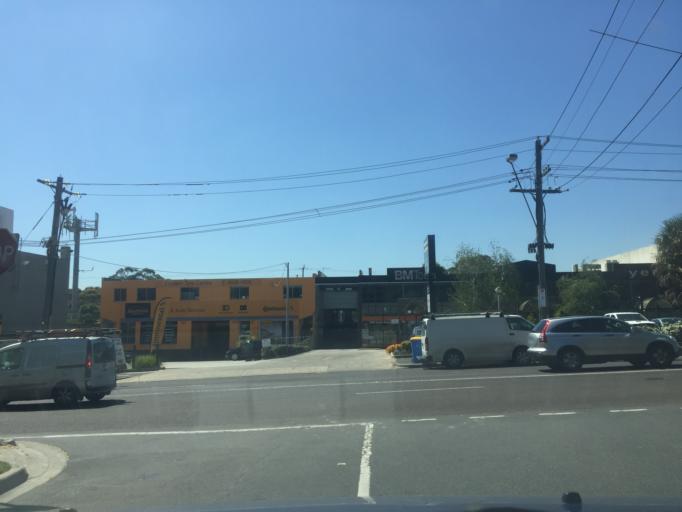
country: AU
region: Victoria
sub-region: Boroondara
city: Canterbury
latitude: -37.8246
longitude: 145.0844
